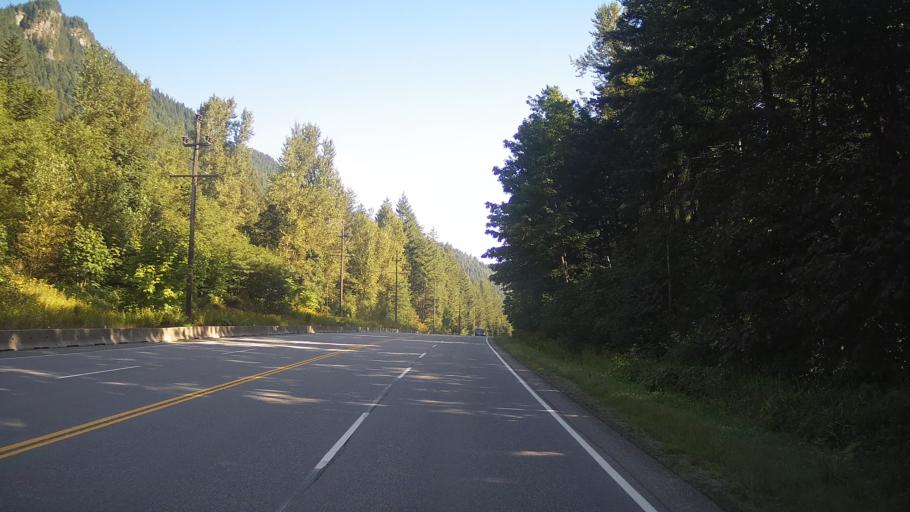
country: CA
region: British Columbia
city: Hope
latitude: 49.4490
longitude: -121.4374
